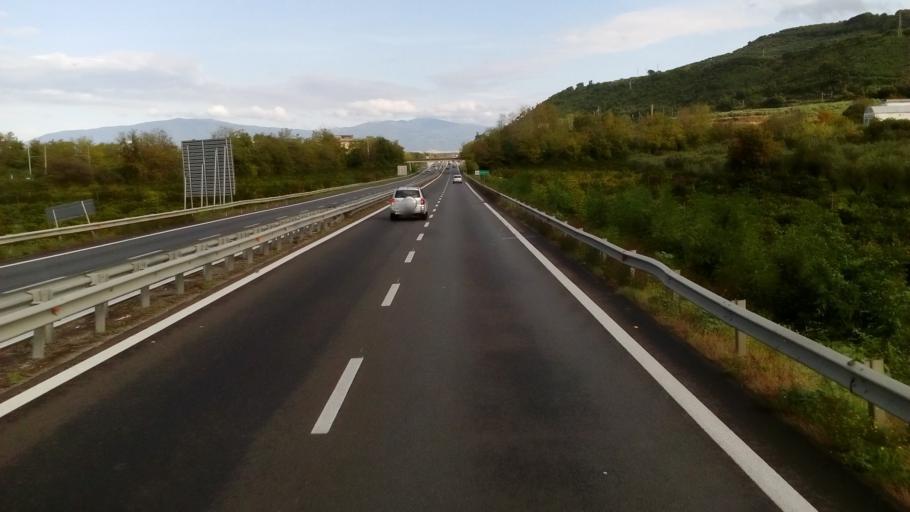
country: IT
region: Calabria
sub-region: Provincia di Vibo-Valentia
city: Pizzo
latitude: 38.7746
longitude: 16.2149
